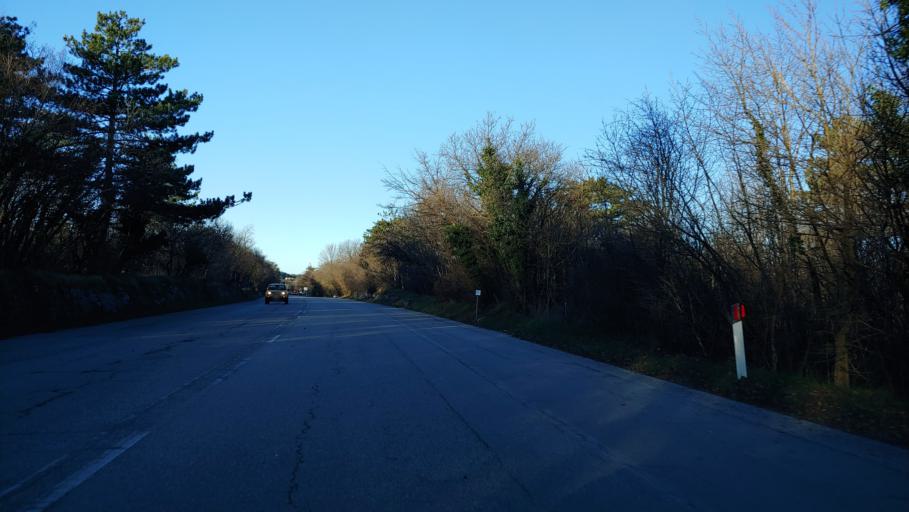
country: IT
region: Friuli Venezia Giulia
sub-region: Provincia di Trieste
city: Villa Opicina
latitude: 45.6804
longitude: 13.8025
